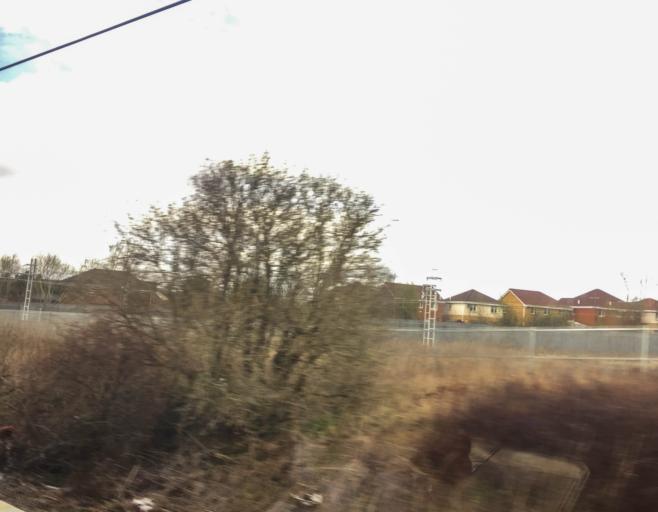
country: GB
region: Scotland
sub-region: North Lanarkshire
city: Holytown
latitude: 55.8079
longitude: -3.9612
